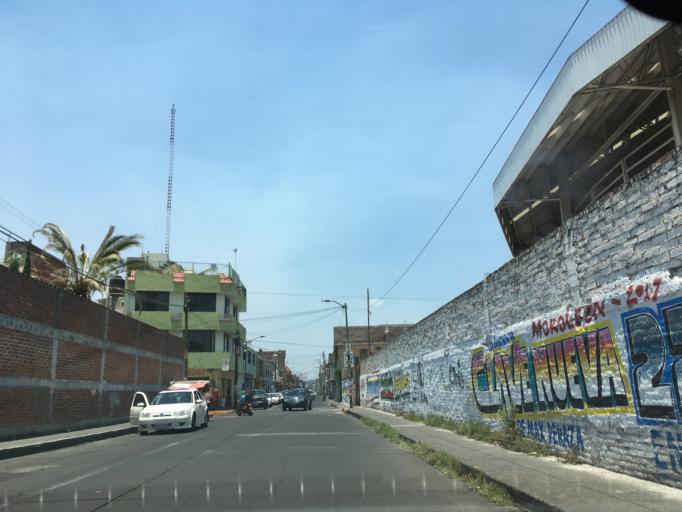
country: MX
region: Guanajuato
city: Uriangato
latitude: 20.1314
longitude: -101.1826
